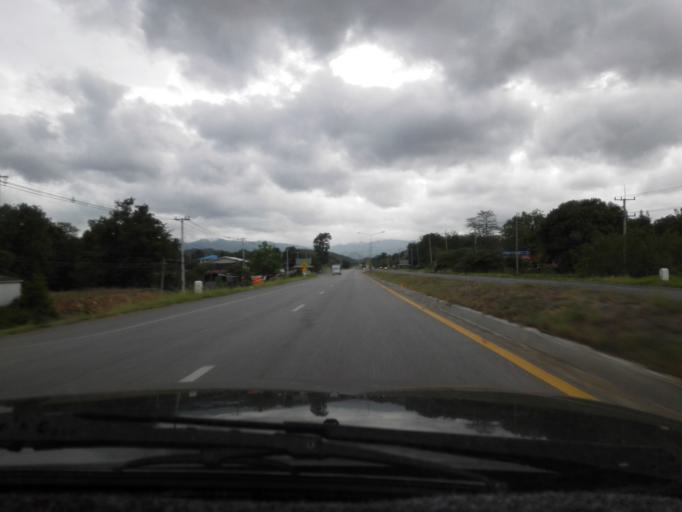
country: TH
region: Tak
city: Tak
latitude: 16.8326
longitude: 99.0980
